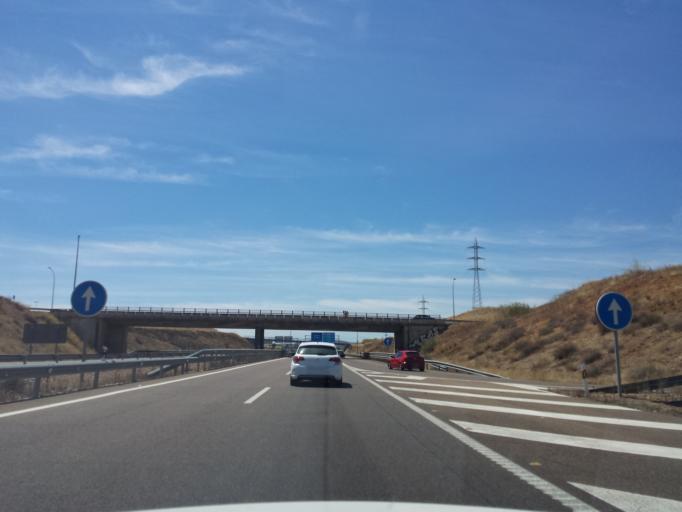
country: ES
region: Extremadura
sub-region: Provincia de Badajoz
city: Merida
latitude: 38.9229
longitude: -6.3714
